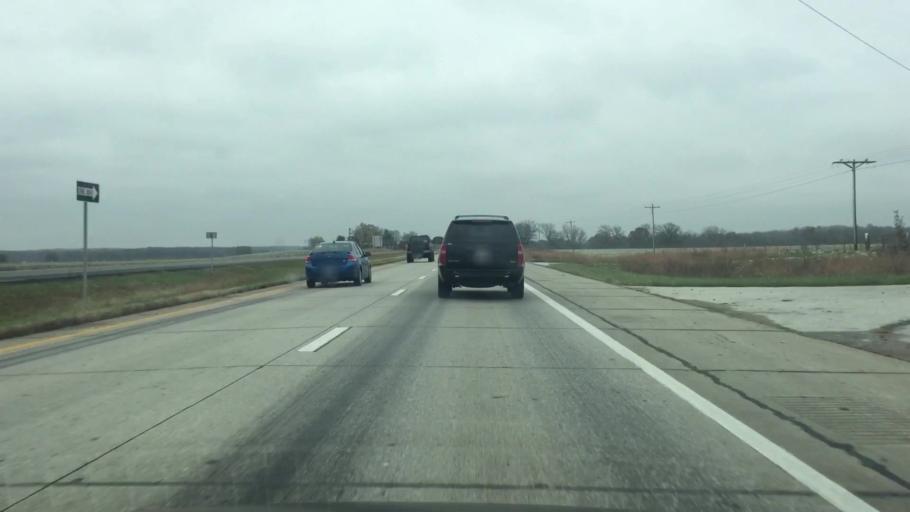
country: US
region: Missouri
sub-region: Saint Clair County
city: Osceola
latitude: 38.0316
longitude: -93.6769
